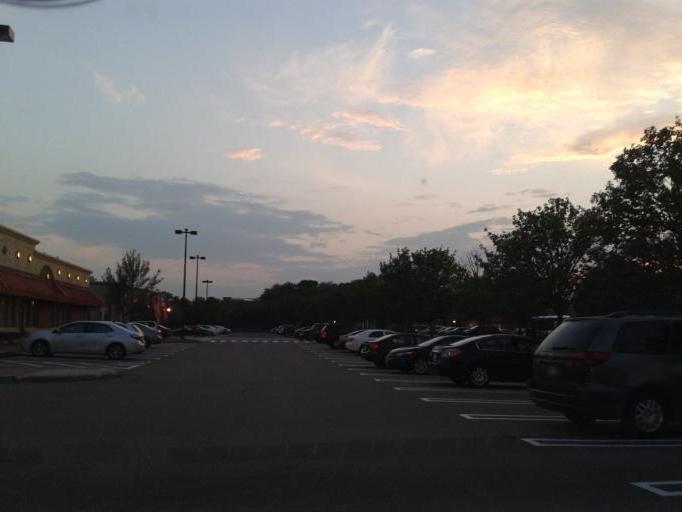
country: US
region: Massachusetts
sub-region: Middlesex County
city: Framingham
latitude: 42.2996
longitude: -71.3940
